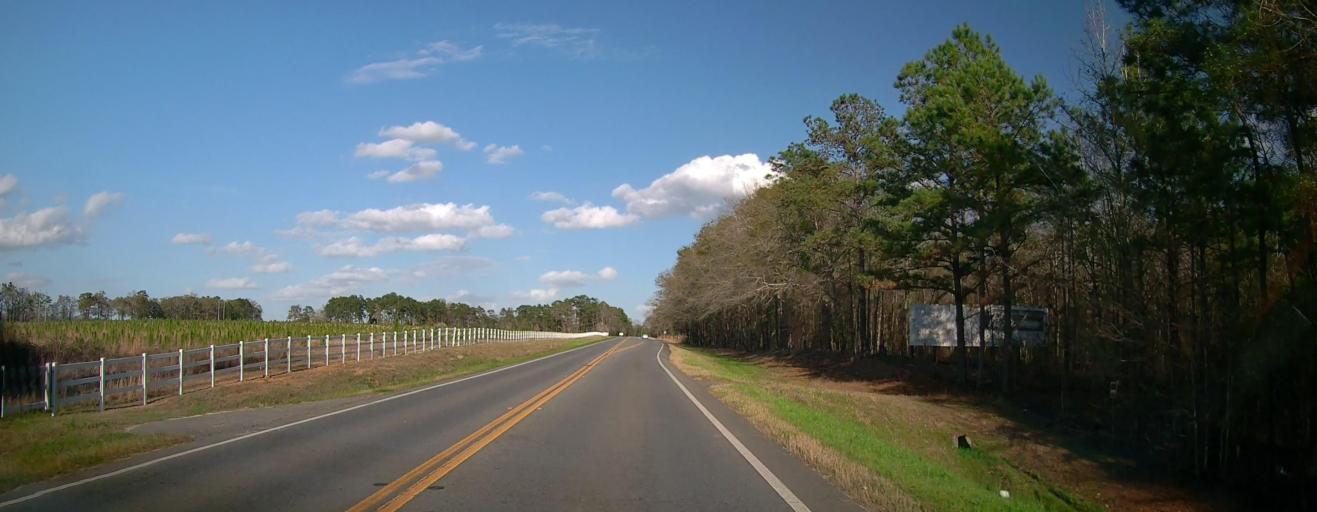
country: US
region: Georgia
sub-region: Toombs County
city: Vidalia
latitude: 32.2145
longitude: -82.4556
